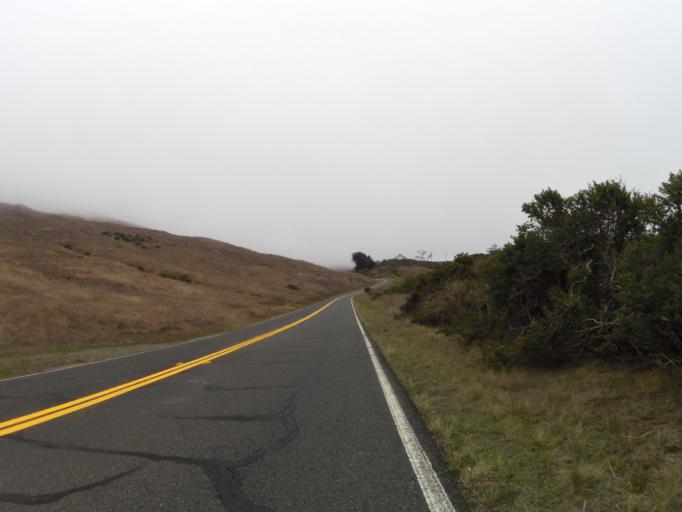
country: US
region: California
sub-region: Sonoma County
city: Monte Rio
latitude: 38.5082
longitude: -123.2276
